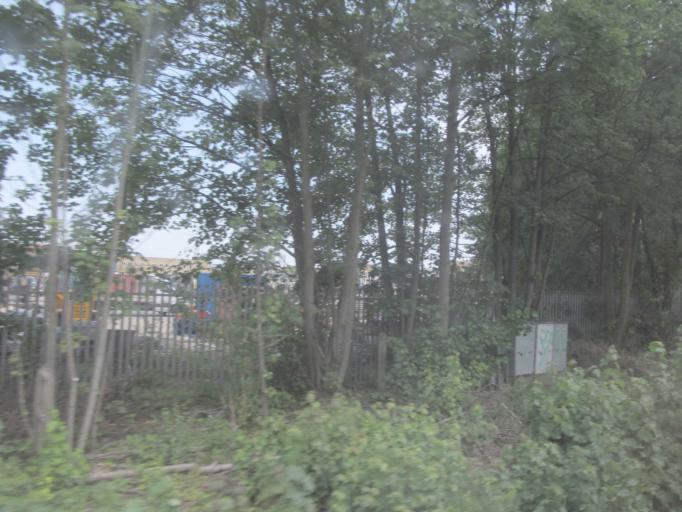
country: GB
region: England
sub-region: Slough
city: Slough
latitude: 51.5109
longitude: -0.5794
